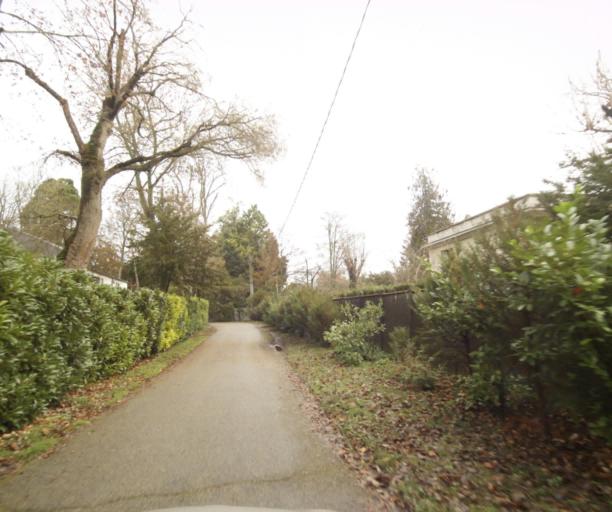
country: FR
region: Ile-de-France
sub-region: Departement de Seine-et-Marne
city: Avon
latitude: 48.4102
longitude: 2.7197
